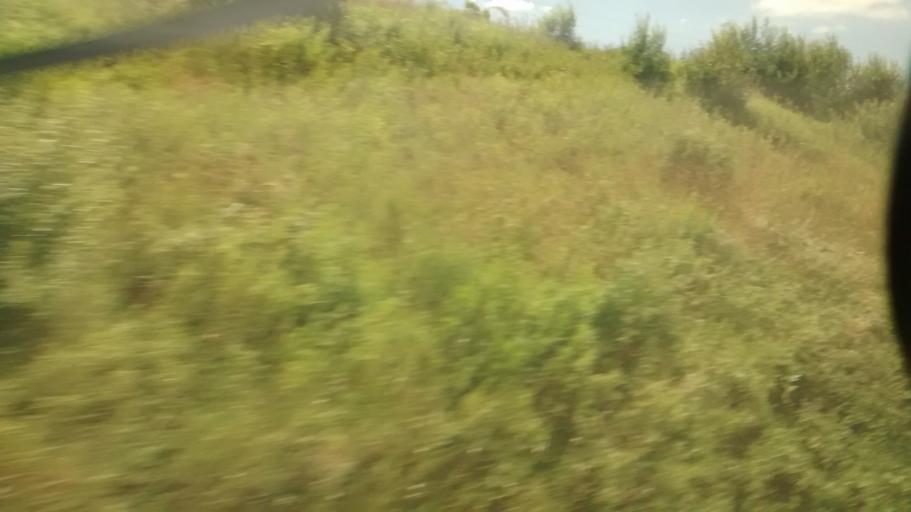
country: FR
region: Rhone-Alpes
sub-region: Departement de l'Ain
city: Beynost
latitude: 45.8539
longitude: 4.9988
